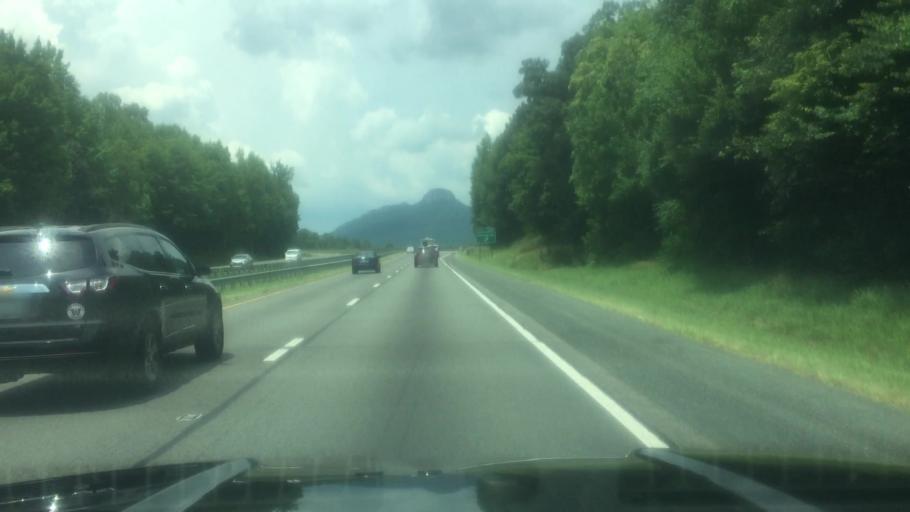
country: US
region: North Carolina
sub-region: Surry County
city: Pilot Mountain
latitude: 36.3141
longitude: -80.4335
